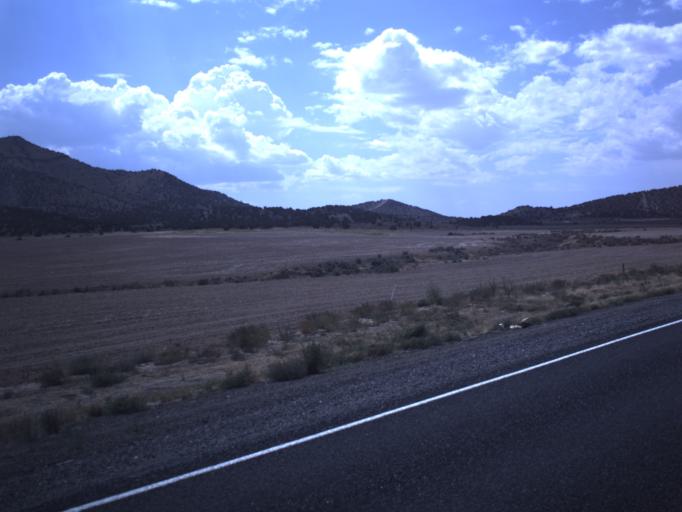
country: US
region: Utah
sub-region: Utah County
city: Eagle Mountain
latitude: 40.2399
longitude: -112.1526
